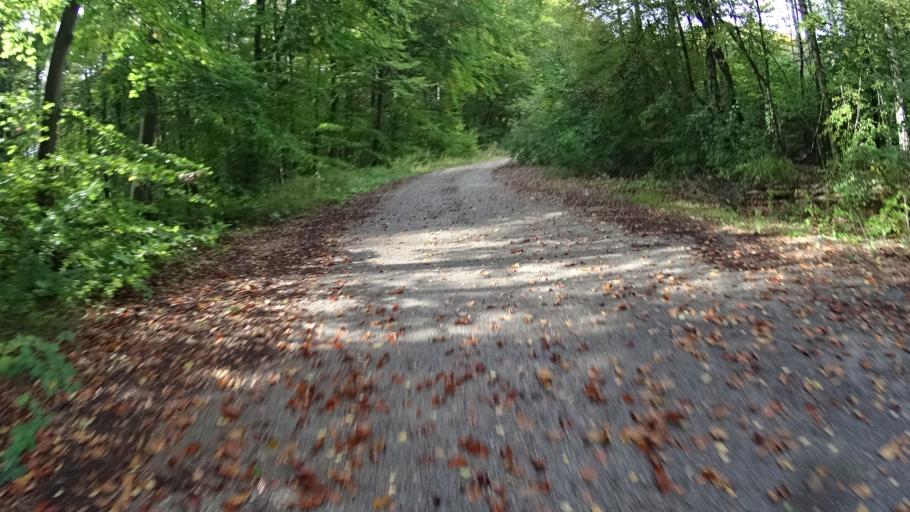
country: DE
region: Bavaria
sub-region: Upper Bavaria
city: Walting
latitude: 48.9044
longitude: 11.3241
